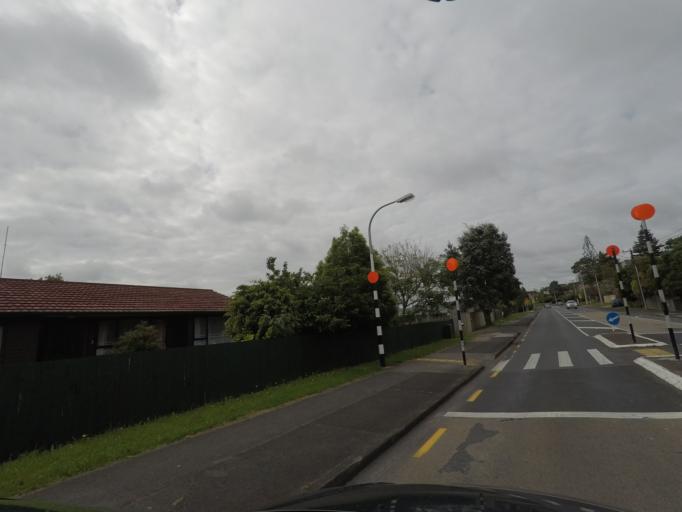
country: NZ
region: Auckland
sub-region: Auckland
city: Rosebank
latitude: -36.8507
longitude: 174.6101
